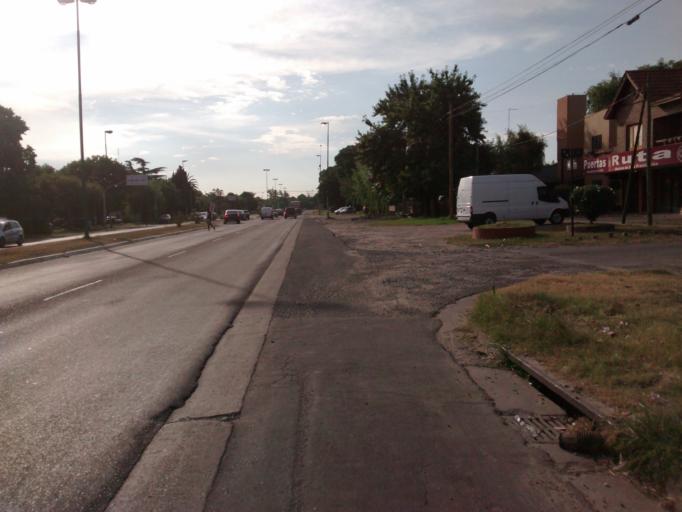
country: AR
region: Buenos Aires
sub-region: Partido de La Plata
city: La Plata
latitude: -34.8506
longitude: -58.0903
